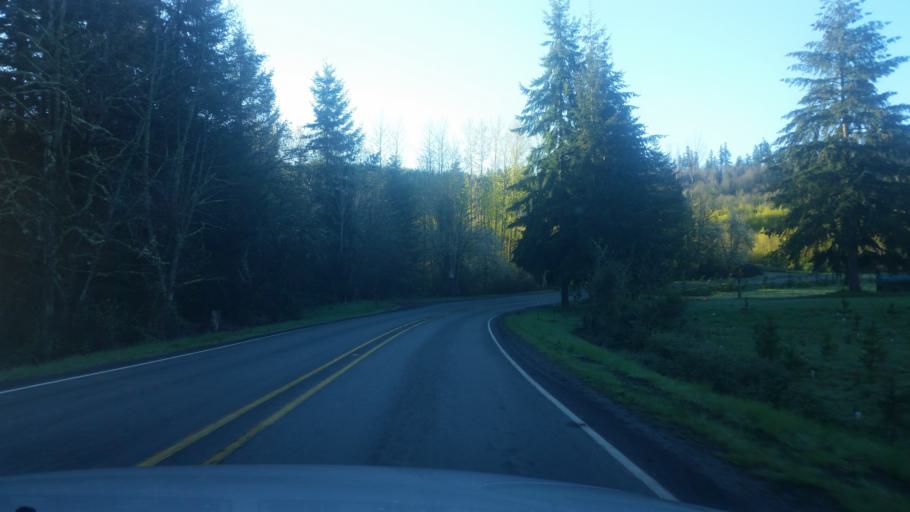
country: US
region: Washington
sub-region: Pierce County
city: Eatonville
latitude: 46.8632
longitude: -122.2518
